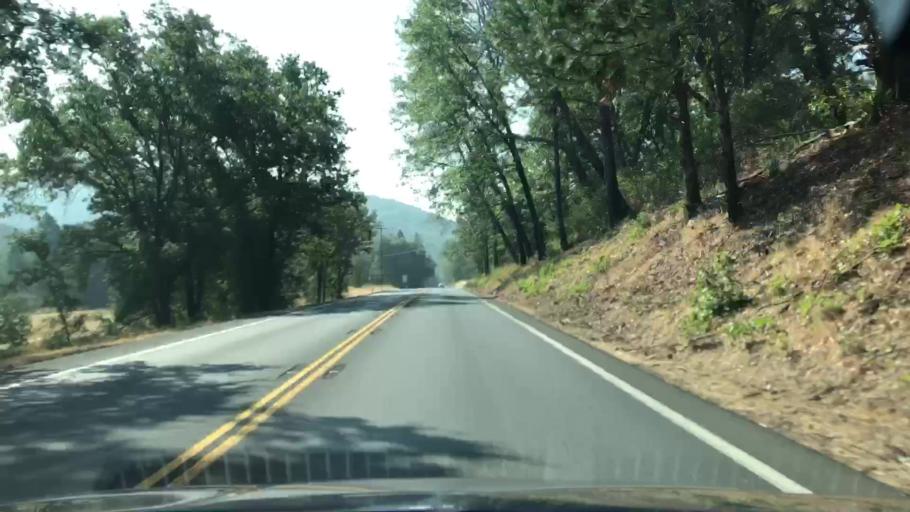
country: US
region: California
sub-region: Lake County
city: Middletown
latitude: 38.7027
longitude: -122.6042
